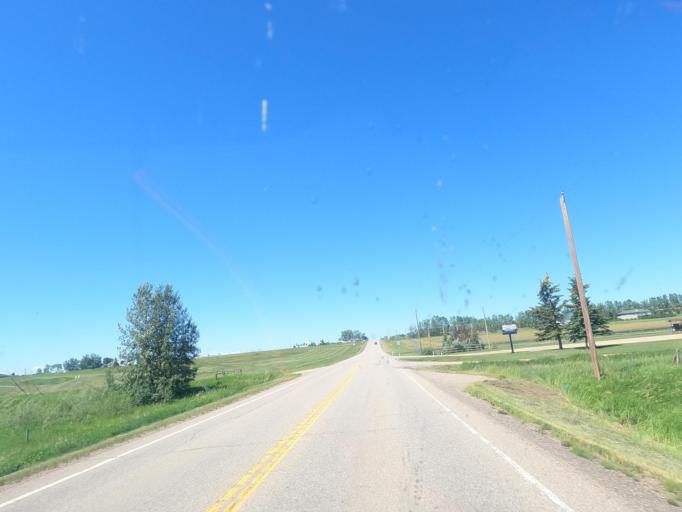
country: CA
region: Alberta
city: Chestermere
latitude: 51.1544
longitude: -113.7656
